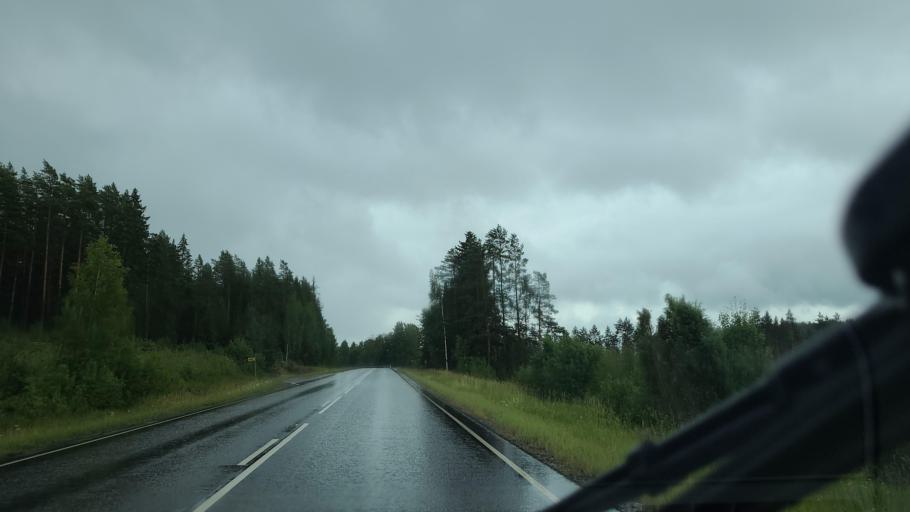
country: FI
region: Varsinais-Suomi
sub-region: Aboland-Turunmaa
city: Kimito
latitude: 60.2068
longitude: 22.6451
